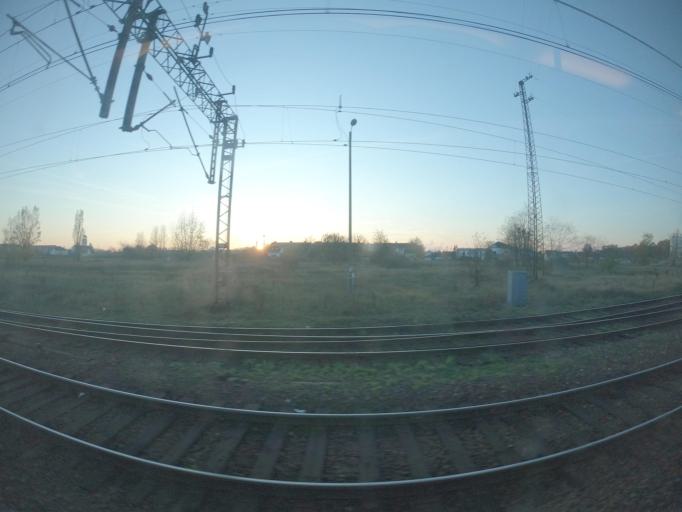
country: PL
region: Lubusz
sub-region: Powiat gorzowski
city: Kostrzyn nad Odra
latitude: 52.6012
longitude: 14.6467
